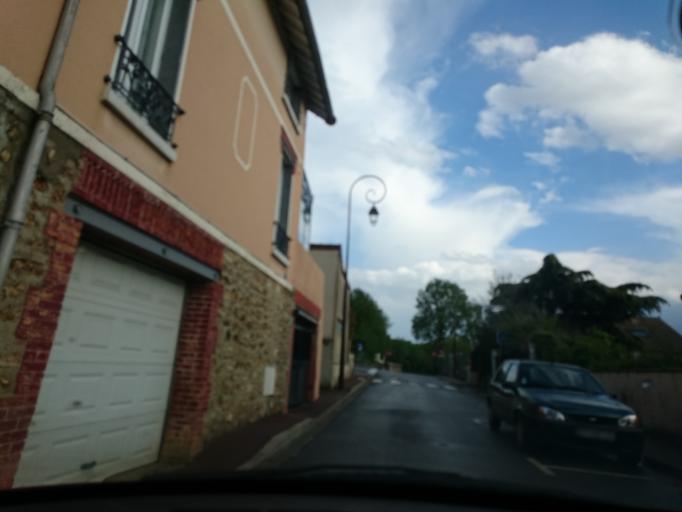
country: FR
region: Ile-de-France
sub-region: Departement de l'Essonne
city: Etiolles
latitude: 48.6313
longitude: 2.4724
